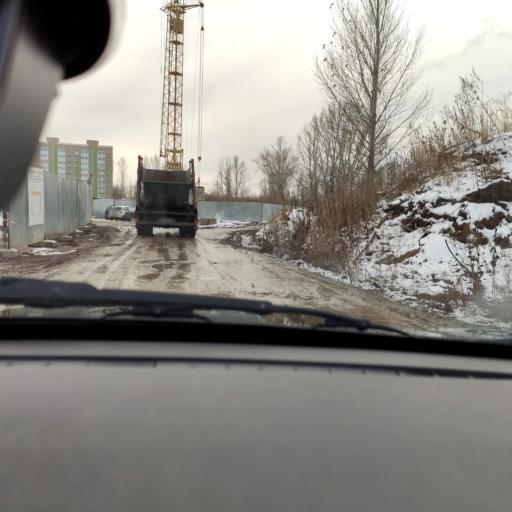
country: RU
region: Samara
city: Tol'yatti
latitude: 53.5493
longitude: 49.3105
